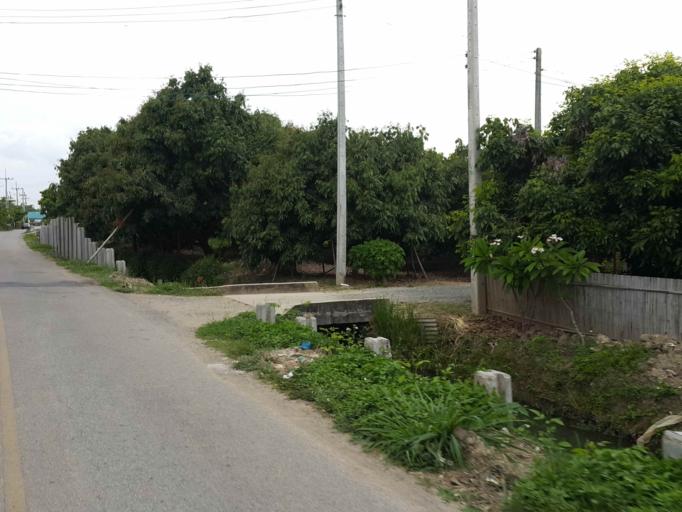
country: TH
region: Chiang Mai
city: Saraphi
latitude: 18.6974
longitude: 99.0279
